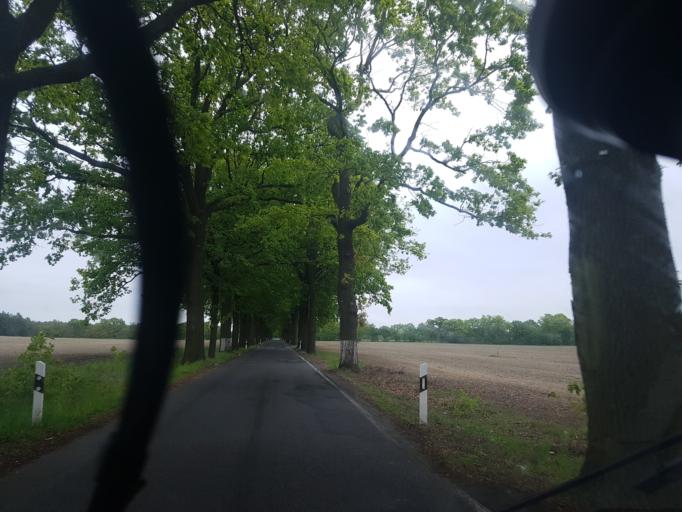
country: DE
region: Brandenburg
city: Neupetershain
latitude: 51.6098
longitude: 14.1447
